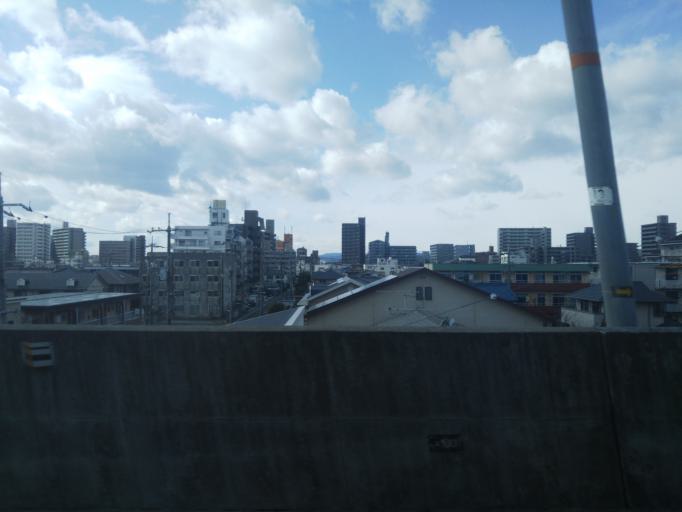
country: JP
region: Okayama
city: Okayama-shi
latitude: 34.6456
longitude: 133.9110
